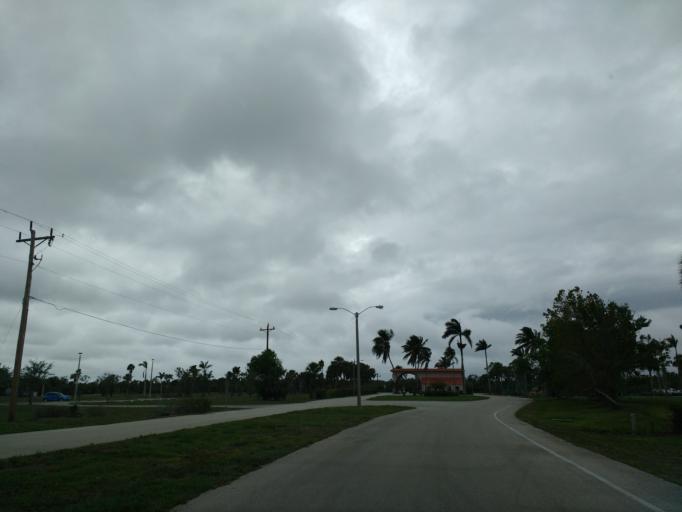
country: US
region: Florida
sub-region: Collier County
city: Marco
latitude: 25.9574
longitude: -81.5122
